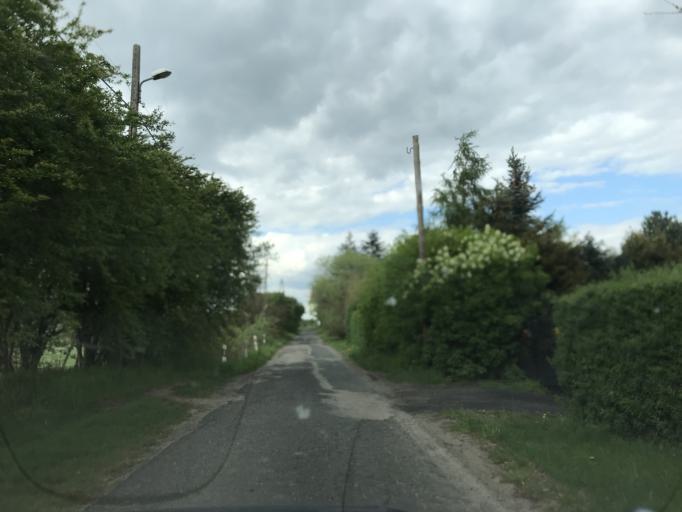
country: PL
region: West Pomeranian Voivodeship
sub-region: Powiat mysliborski
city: Mysliborz
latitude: 52.8873
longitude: 14.8971
